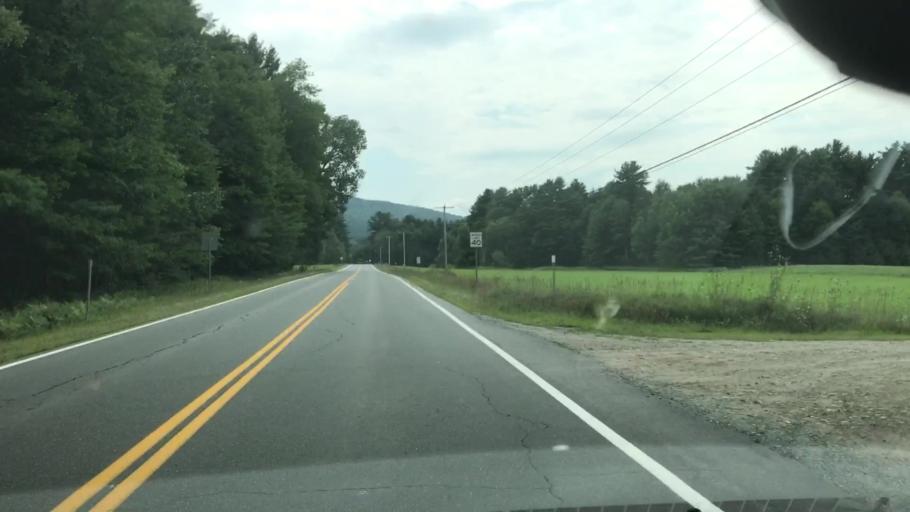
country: US
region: New Hampshire
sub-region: Grafton County
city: Woodsville
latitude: 44.2546
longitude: -72.0507
